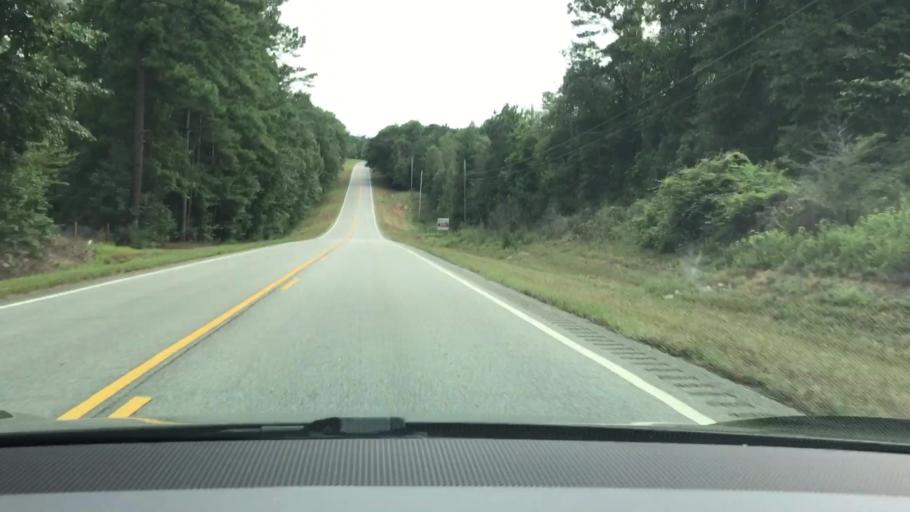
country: US
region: Alabama
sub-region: Pike County
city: Troy
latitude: 31.6236
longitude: -85.9780
